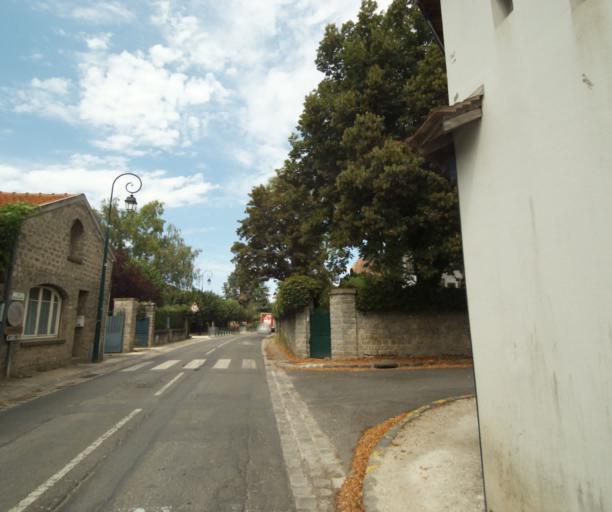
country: FR
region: Ile-de-France
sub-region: Departement de Seine-et-Marne
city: Barbizon
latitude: 48.4471
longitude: 2.6019
